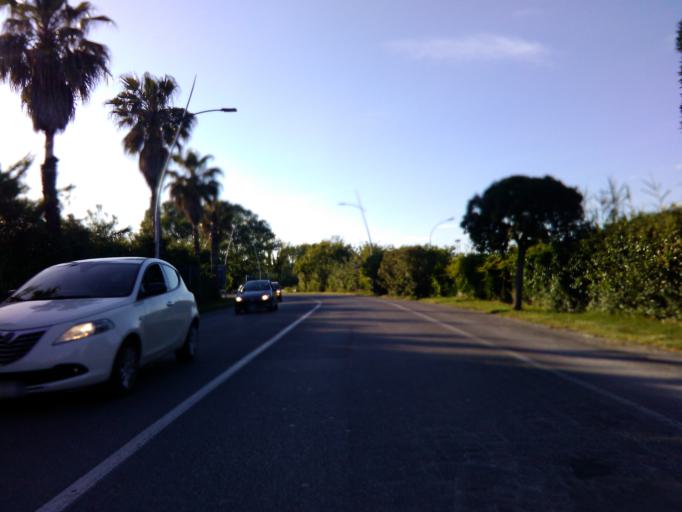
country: IT
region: Tuscany
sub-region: Provincia di Massa-Carrara
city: Marina di Carrara
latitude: 44.0459
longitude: 10.0221
